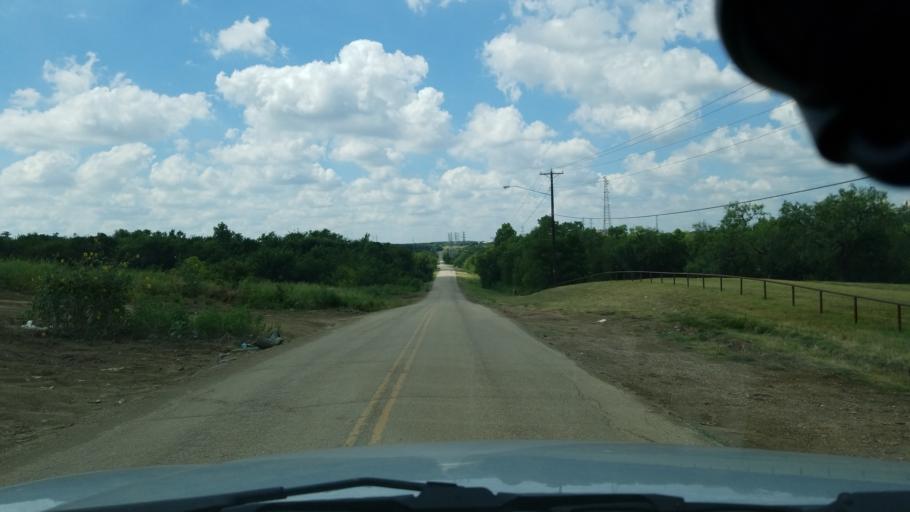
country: US
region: Texas
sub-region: Dallas County
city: Cockrell Hill
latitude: 32.7316
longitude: -96.9309
